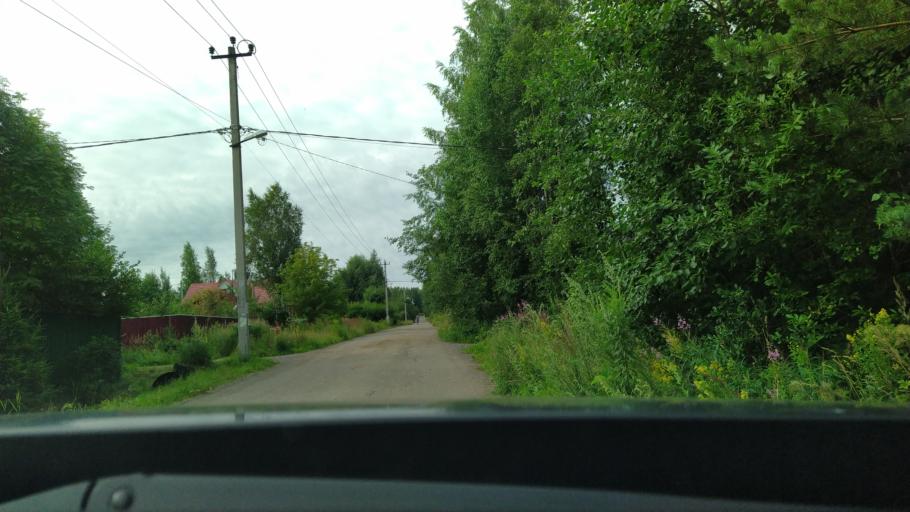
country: RU
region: Leningrad
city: Otradnoye
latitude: 59.7316
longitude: 30.8476
